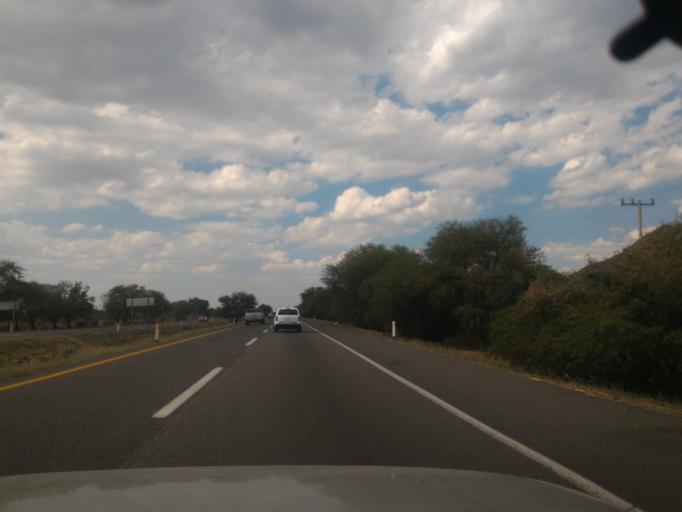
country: MX
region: Jalisco
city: Zacoalco de Torres
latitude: 20.2054
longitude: -103.5268
